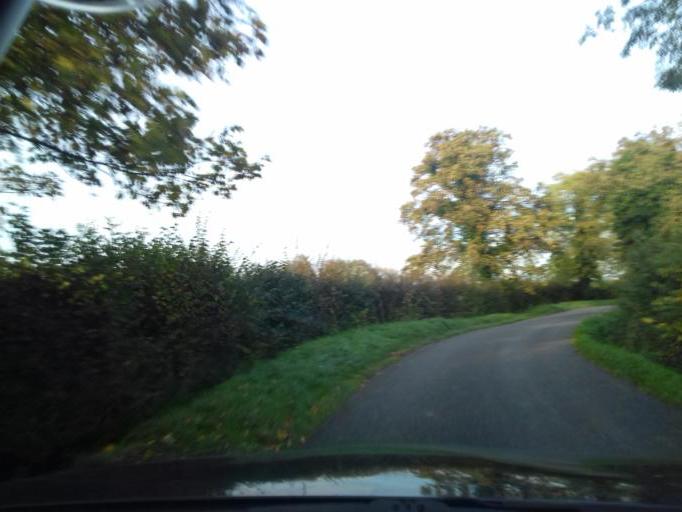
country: IE
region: Leinster
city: Hartstown
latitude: 53.3838
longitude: -6.4424
